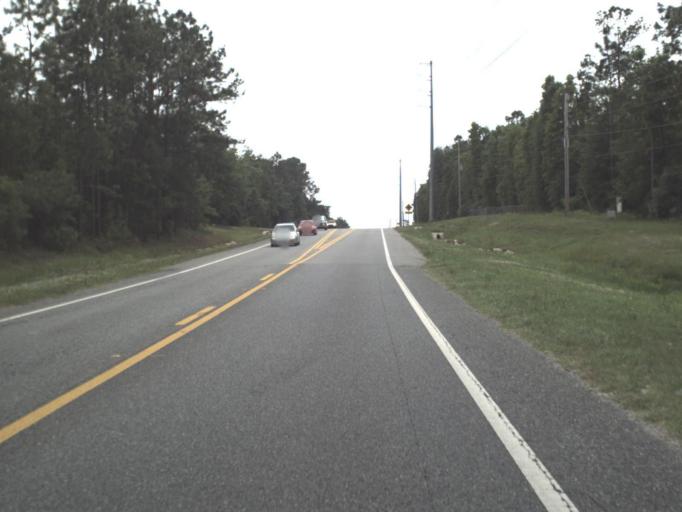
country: US
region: Florida
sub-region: Clay County
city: Middleburg
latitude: 30.0293
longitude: -81.8976
